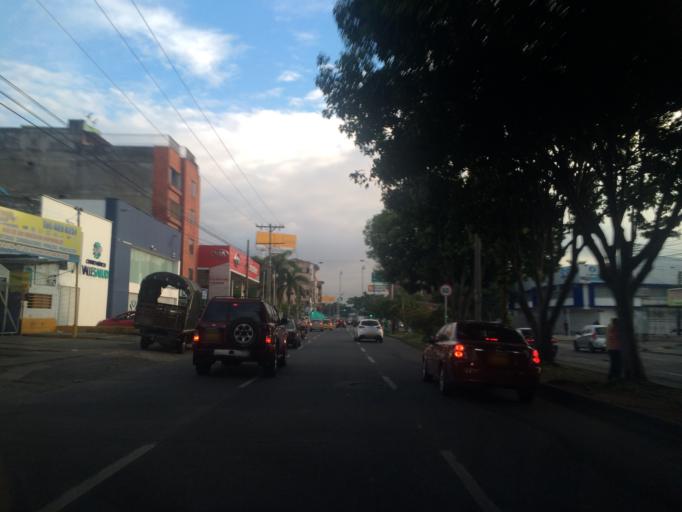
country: CO
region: Valle del Cauca
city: Cali
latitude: 3.4203
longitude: -76.5390
